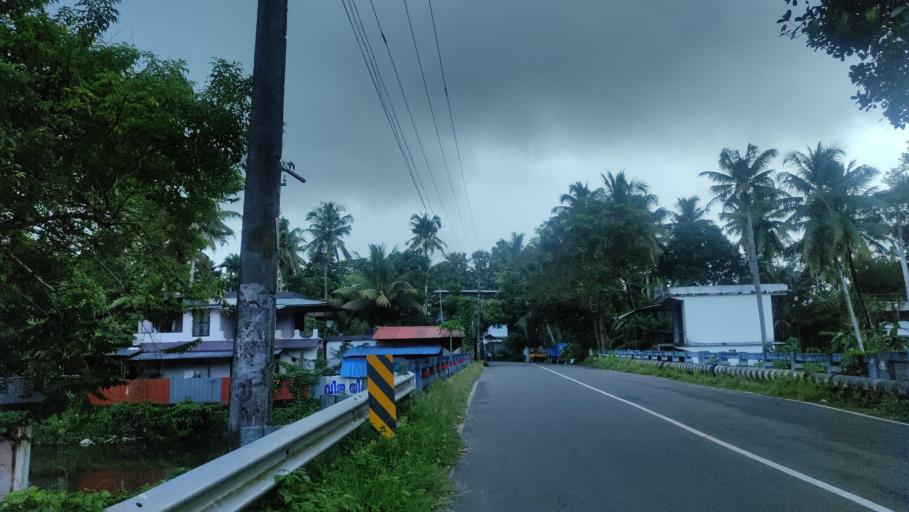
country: IN
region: Kerala
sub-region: Alappuzha
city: Kayankulam
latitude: 9.1940
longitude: 76.5007
